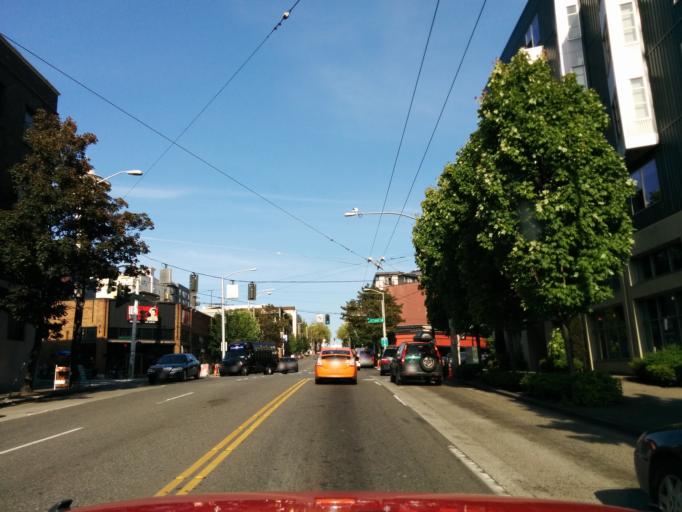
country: US
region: Washington
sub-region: King County
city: Seattle
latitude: 47.6186
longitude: -122.3560
